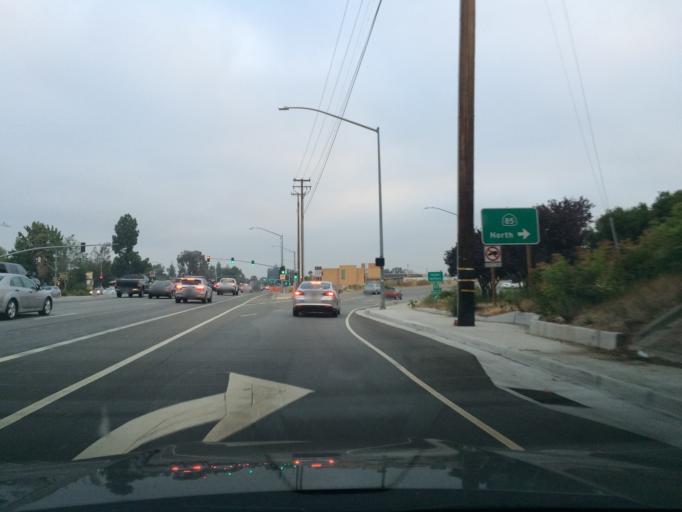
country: US
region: California
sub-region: Santa Clara County
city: Seven Trees
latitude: 37.2559
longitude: -121.8757
